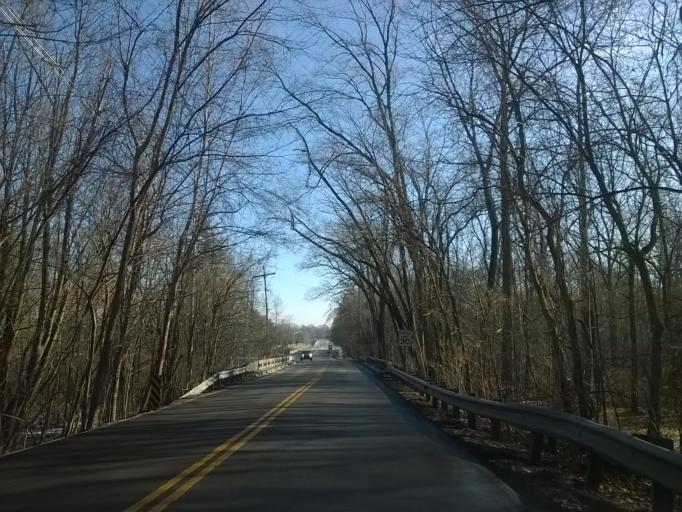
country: US
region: Indiana
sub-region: Hamilton County
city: Carmel
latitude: 39.9856
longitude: -86.1242
